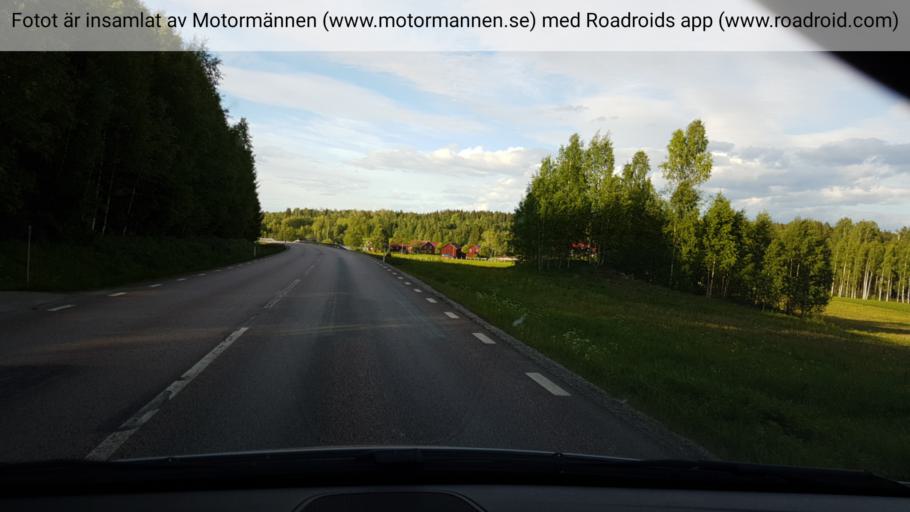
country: SE
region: Vaestmanland
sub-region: Skinnskattebergs Kommun
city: Skinnskatteberg
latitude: 59.8763
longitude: 15.6566
